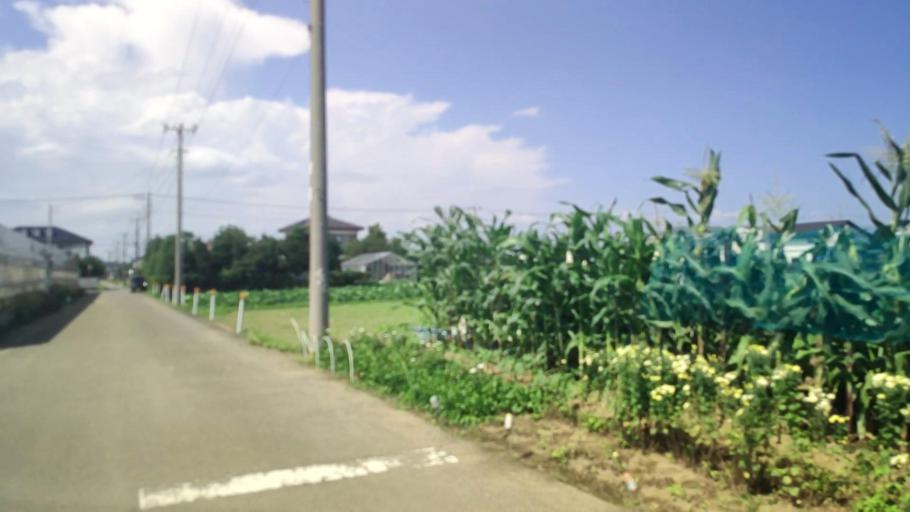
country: JP
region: Kanagawa
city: Isehara
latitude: 35.3652
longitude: 139.3120
